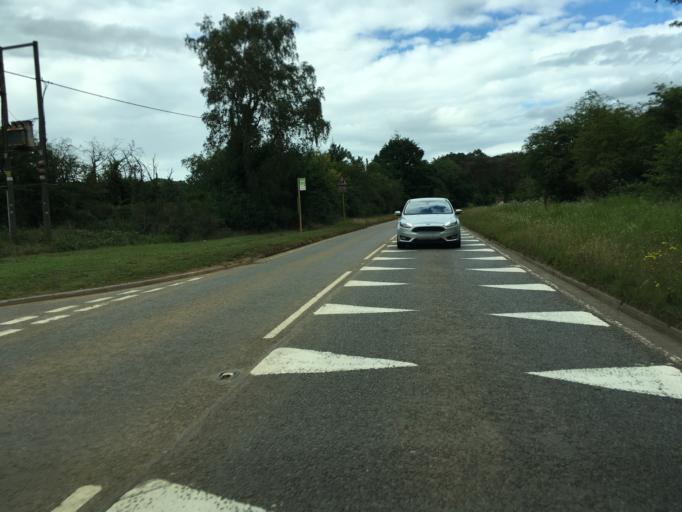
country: GB
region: England
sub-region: Central Bedfordshire
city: Leighton Buzzard
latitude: 51.9516
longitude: -0.6539
